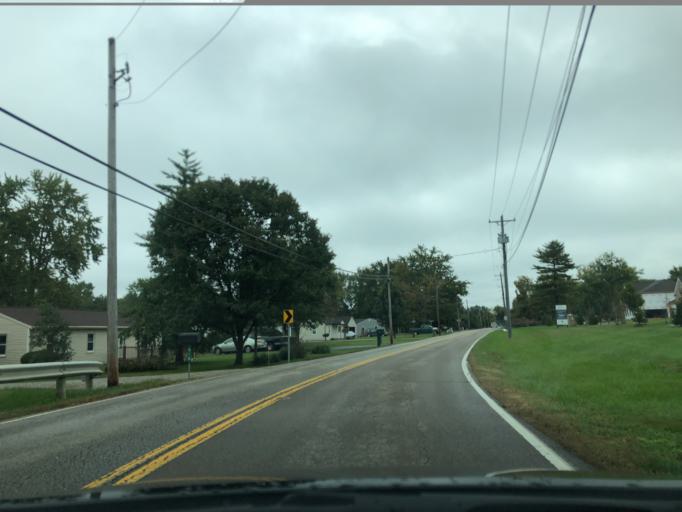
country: US
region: Ohio
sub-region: Hamilton County
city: The Village of Indian Hill
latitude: 39.2337
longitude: -84.2717
